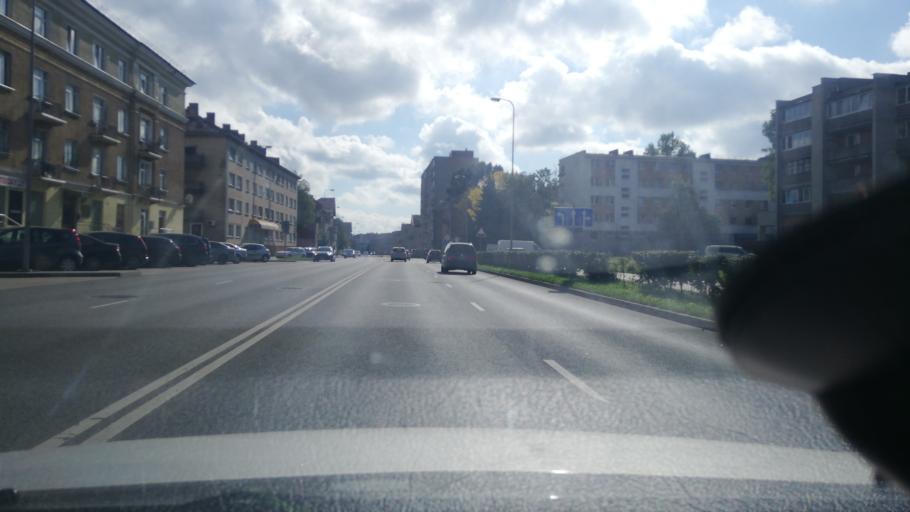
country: LT
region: Klaipedos apskritis
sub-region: Klaipeda
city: Klaipeda
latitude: 55.6819
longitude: 21.1507
